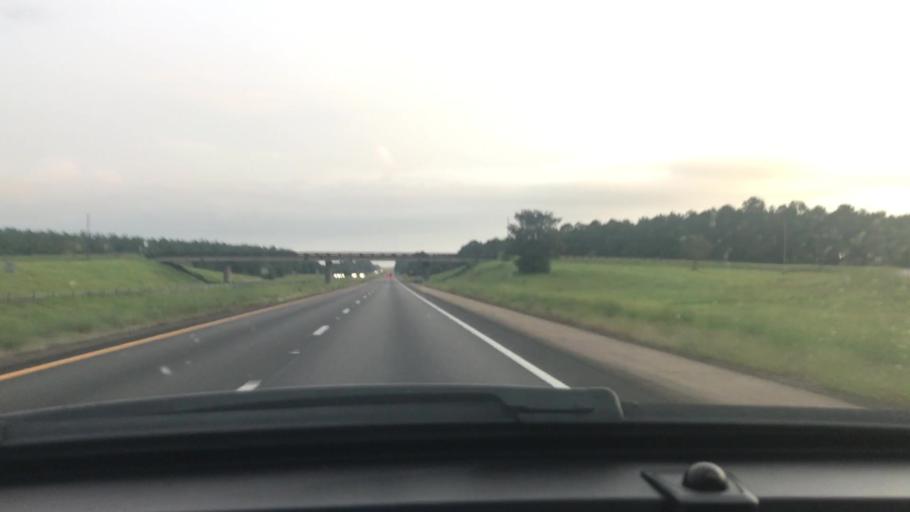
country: US
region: Louisiana
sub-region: Tangipahoa Parish
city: Kentwood
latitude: 31.0130
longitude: -90.5032
